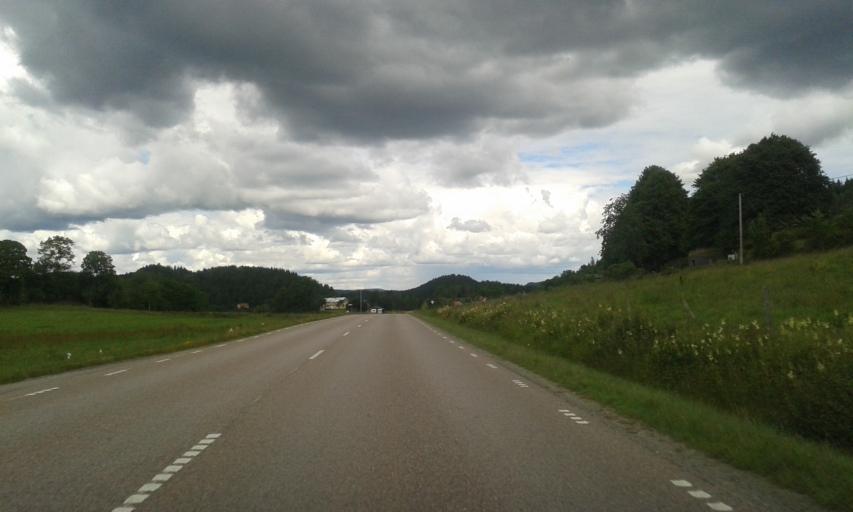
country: SE
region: Vaestra Goetaland
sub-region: Lilla Edets Kommun
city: Lilla Edet
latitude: 58.0896
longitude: 12.1186
